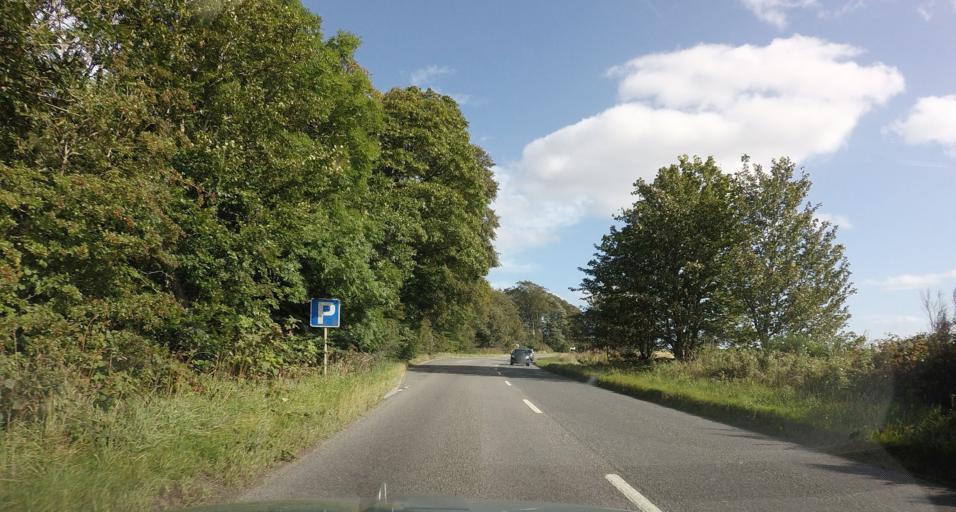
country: GB
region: Scotland
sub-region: Aberdeenshire
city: Westhill
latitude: 57.1551
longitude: -2.3237
